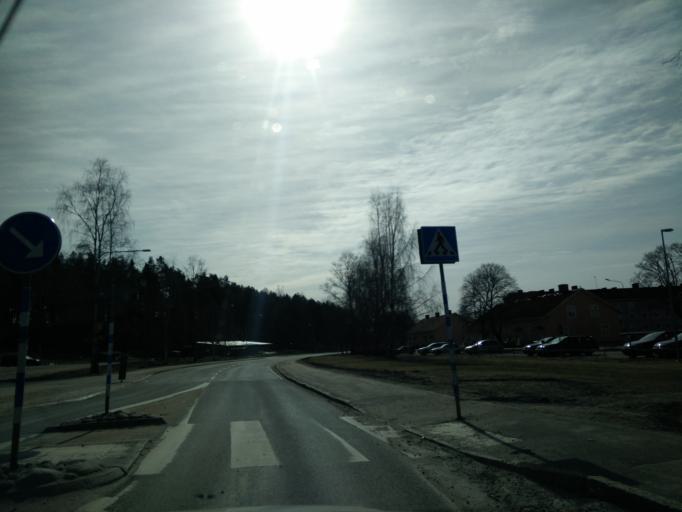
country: SE
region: Vaermland
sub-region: Hagfors Kommun
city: Hagfors
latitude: 60.0343
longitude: 13.7057
